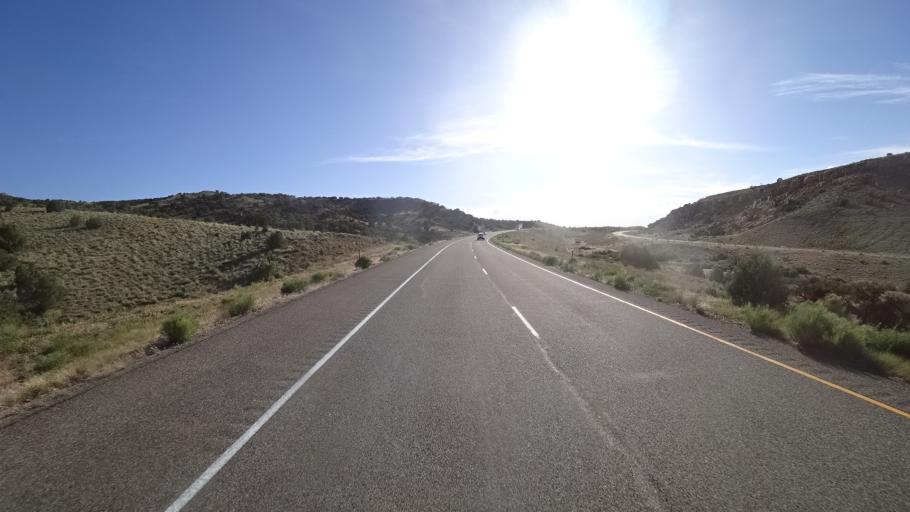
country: US
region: Colorado
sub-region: Mesa County
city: Loma
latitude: 39.1878
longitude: -109.0309
